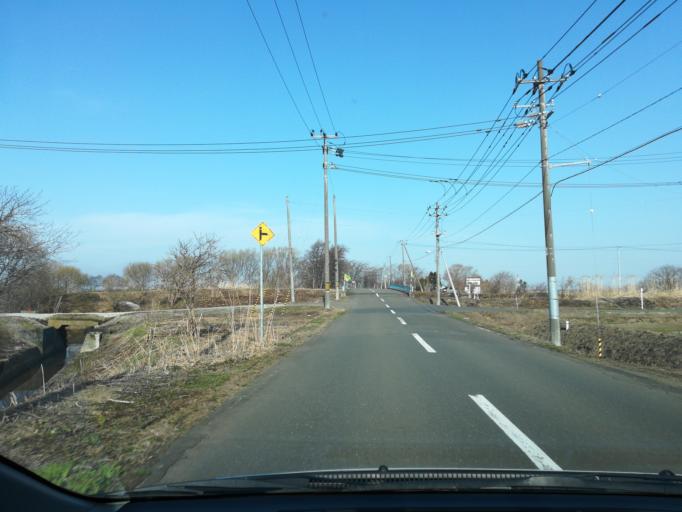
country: JP
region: Hokkaido
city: Ebetsu
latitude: 43.1554
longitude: 141.6416
